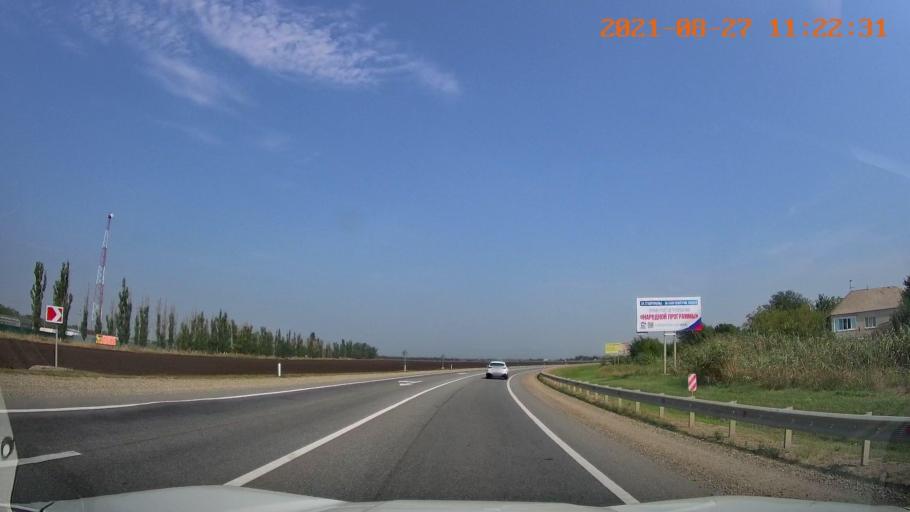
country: RU
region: Stavropol'skiy
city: Barsukovskaya
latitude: 44.6989
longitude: 41.8062
